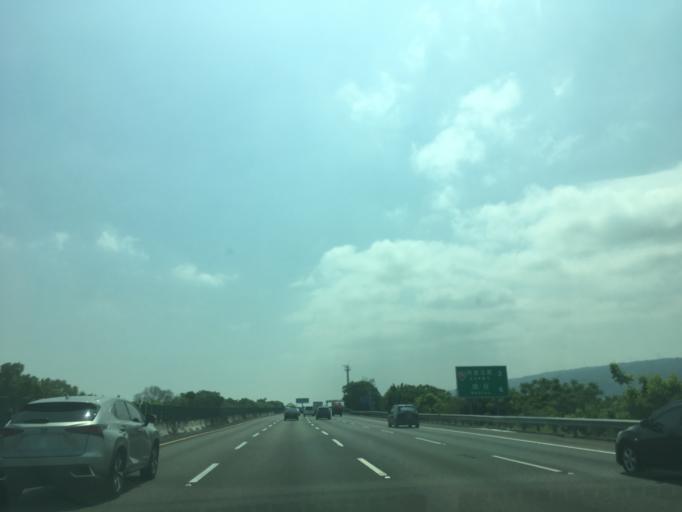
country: TW
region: Taiwan
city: Zhongxing New Village
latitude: 23.9913
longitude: 120.6517
